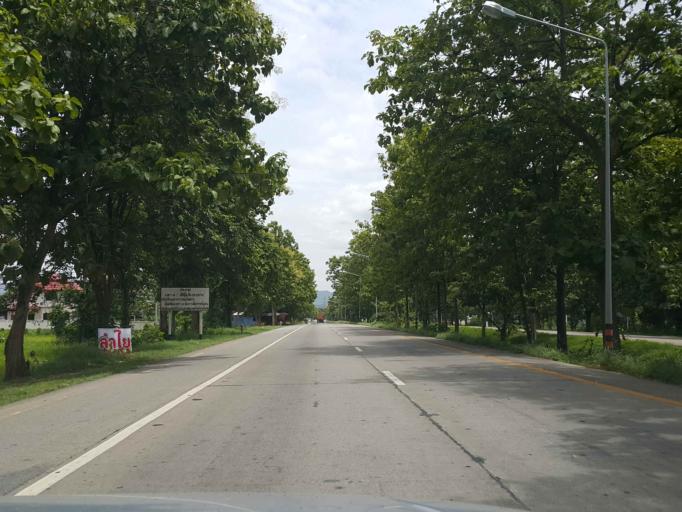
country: TH
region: Lamphun
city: Lamphun
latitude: 18.5420
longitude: 99.0654
